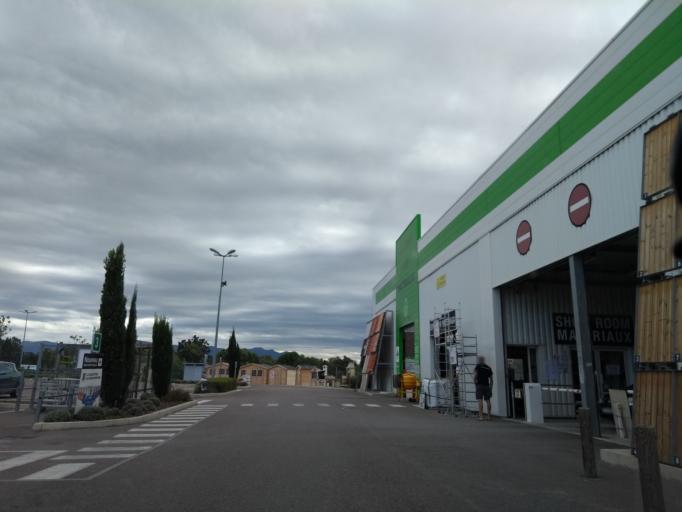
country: FR
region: Languedoc-Roussillon
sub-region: Departement des Pyrenees-Orientales
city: Pollestres
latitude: 42.6686
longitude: 2.8760
